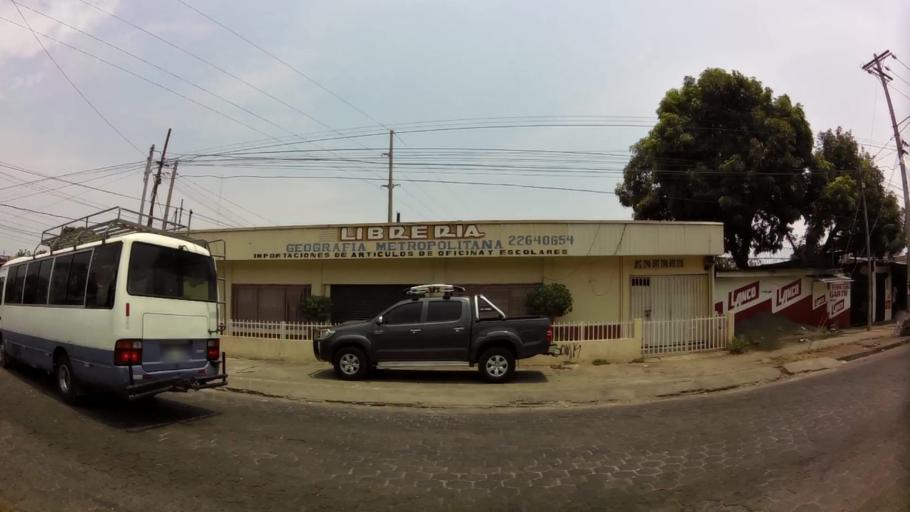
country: NI
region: Managua
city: Ciudad Sandino
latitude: 12.1444
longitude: -86.3047
